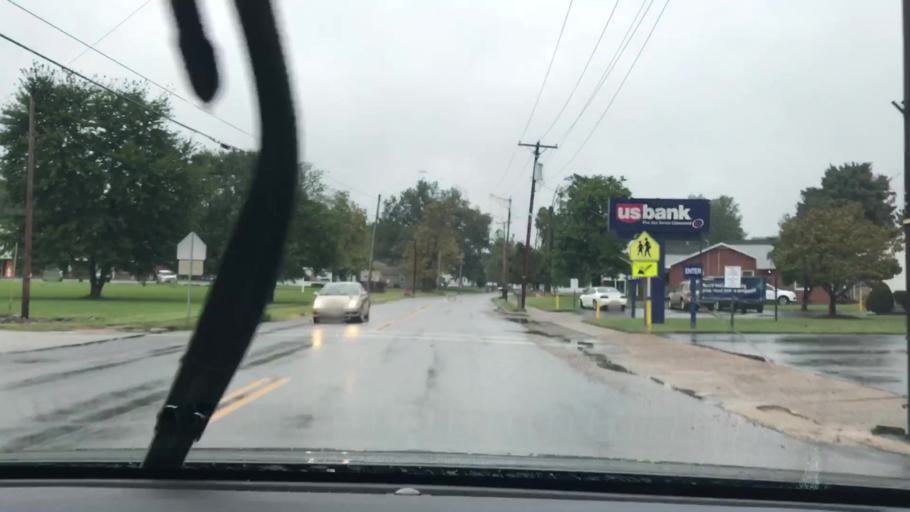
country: US
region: Kentucky
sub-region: McLean County
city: Calhoun
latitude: 37.5425
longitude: -87.2589
